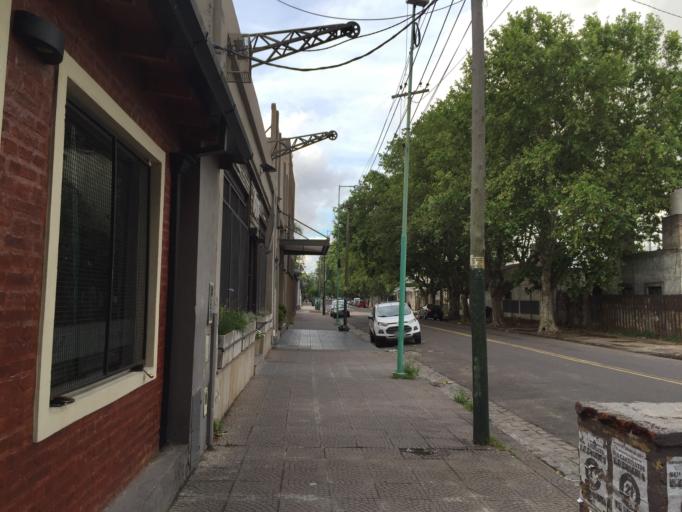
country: AR
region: Buenos Aires
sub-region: Partido de Lomas de Zamora
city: Lomas de Zamora
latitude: -34.7789
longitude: -58.3971
